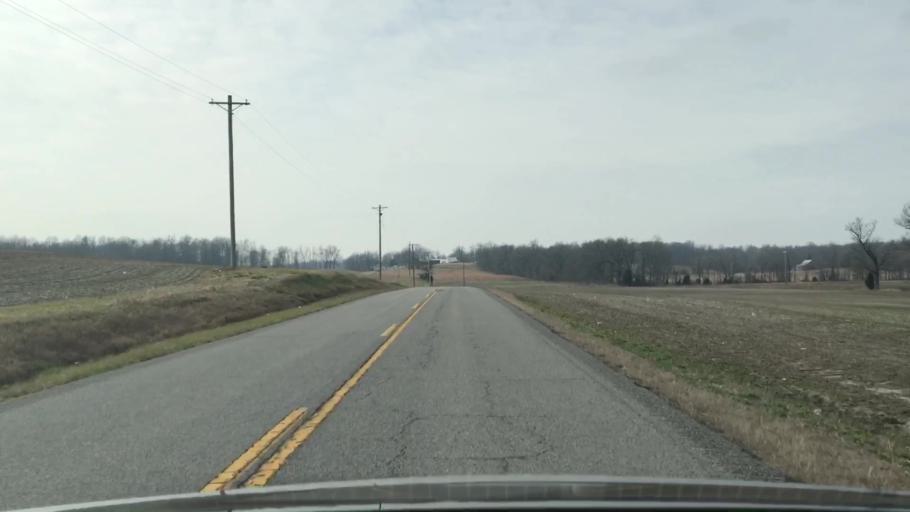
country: US
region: Kentucky
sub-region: Webster County
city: Sebree
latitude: 37.4943
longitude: -87.4532
